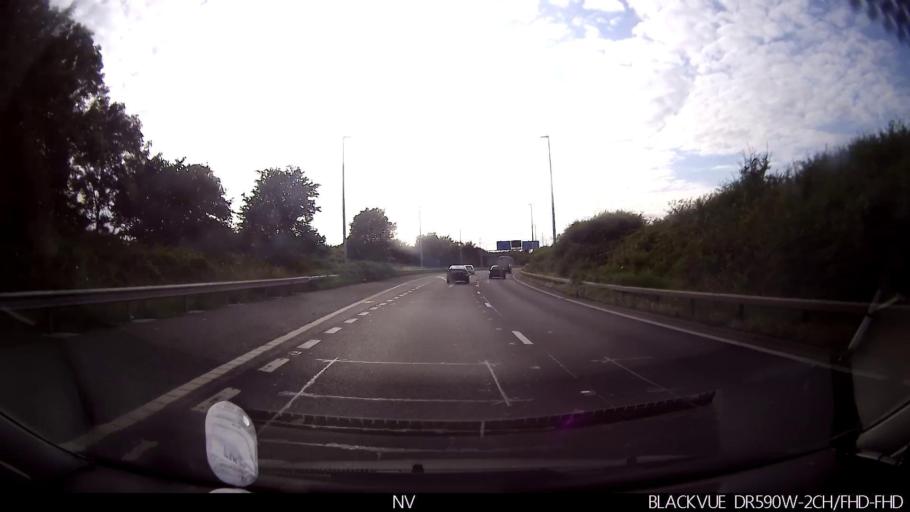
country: GB
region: England
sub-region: City and Borough of Leeds
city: Gildersome
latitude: 53.7453
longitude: -1.6320
